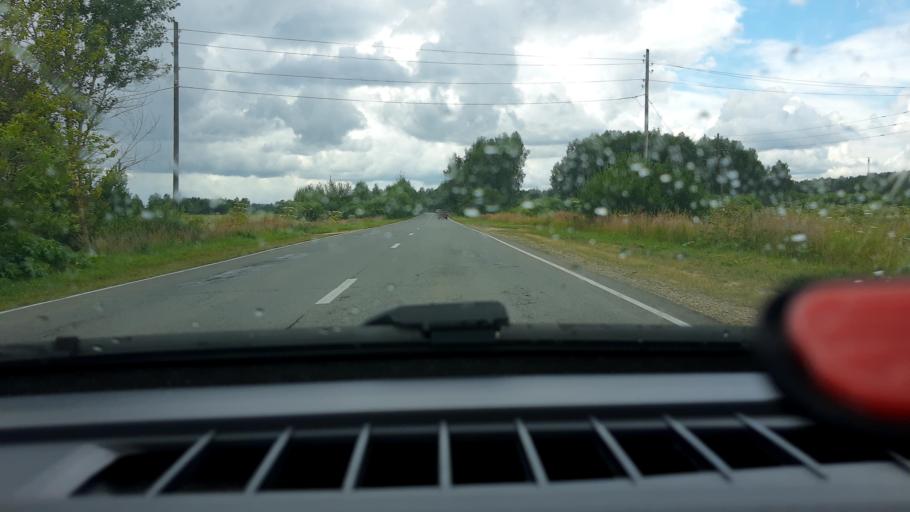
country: RU
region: Nizjnij Novgorod
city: Neklyudovo
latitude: 56.5274
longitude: 43.8426
